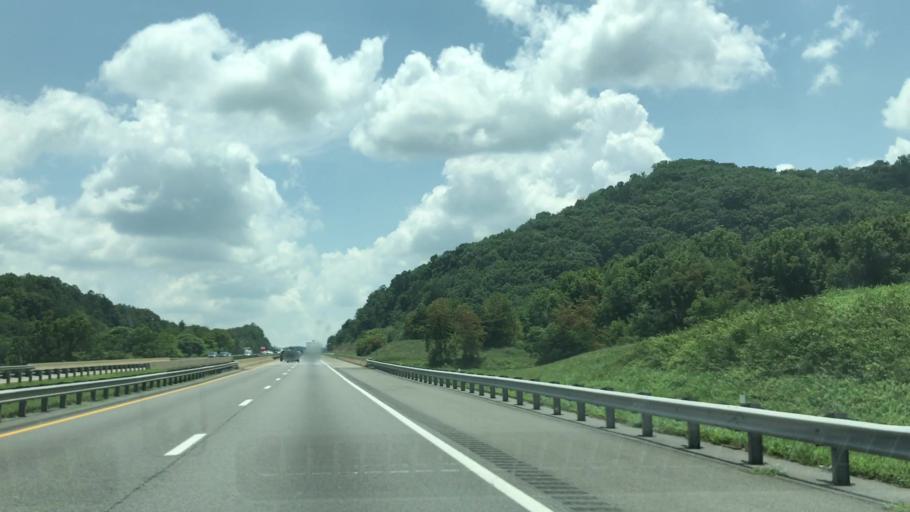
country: US
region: Virginia
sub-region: Carroll County
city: Woodlawn
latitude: 36.8513
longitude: -80.8622
